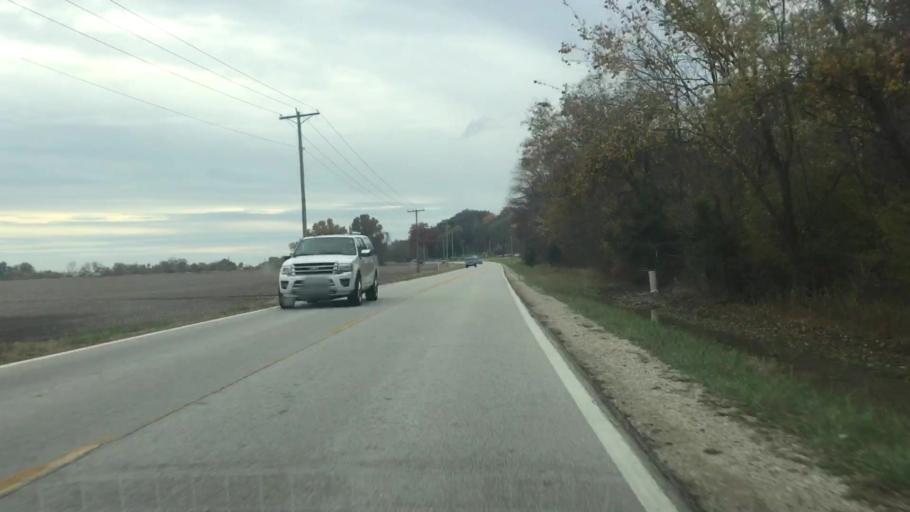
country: US
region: Missouri
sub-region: Gasconade County
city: Hermann
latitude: 38.7220
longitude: -91.5011
